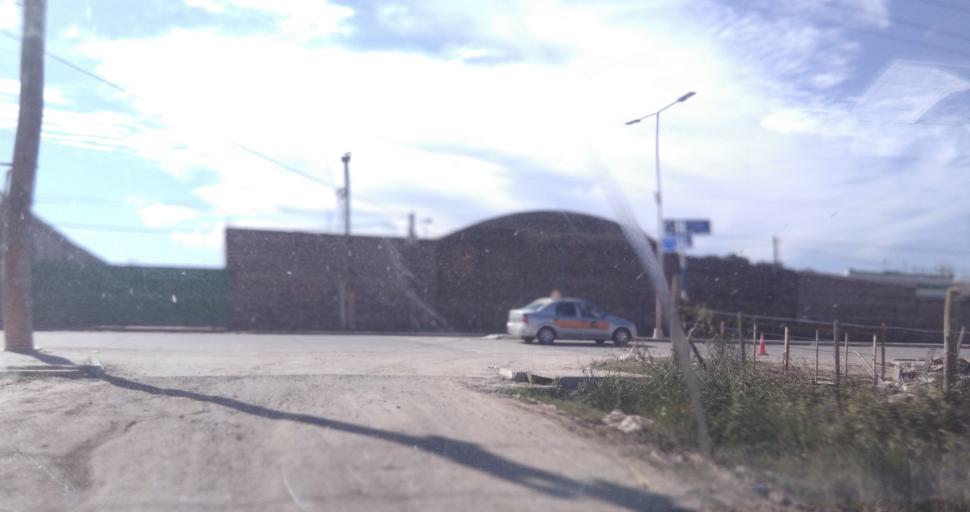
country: AR
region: Chaco
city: Fontana
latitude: -27.4333
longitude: -59.0215
